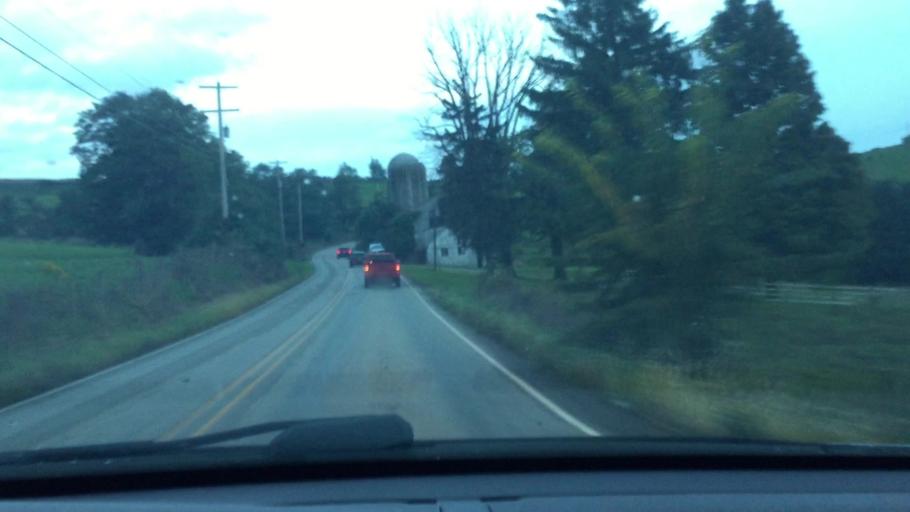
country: US
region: Pennsylvania
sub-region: Washington County
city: McGovern
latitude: 40.2011
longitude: -80.1979
